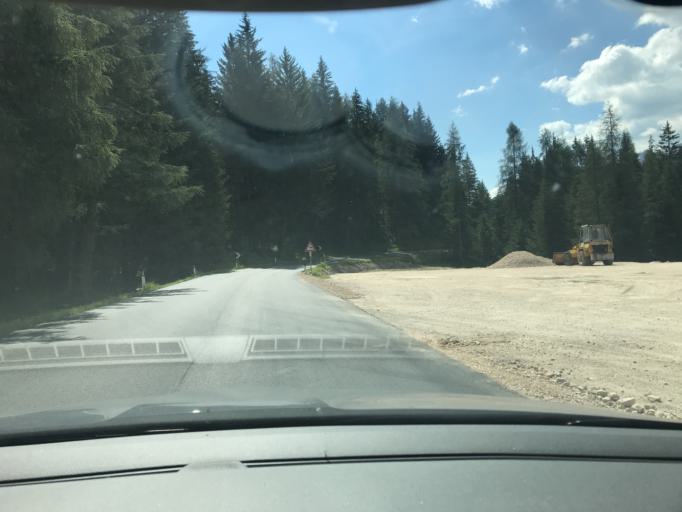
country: IT
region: Veneto
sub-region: Provincia di Belluno
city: Cortina d'Ampezzo
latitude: 46.5225
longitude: 12.0996
